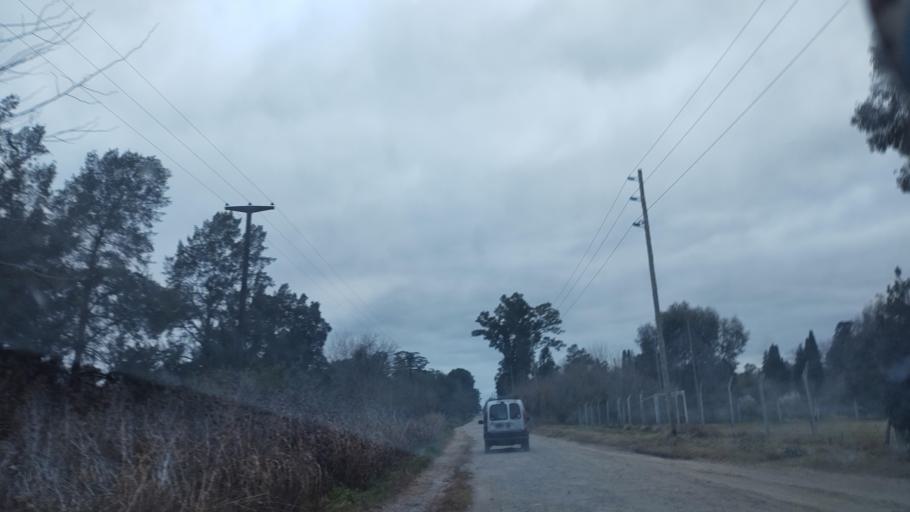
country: AR
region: Buenos Aires
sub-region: Partido de La Plata
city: La Plata
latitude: -34.8639
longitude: -58.1191
